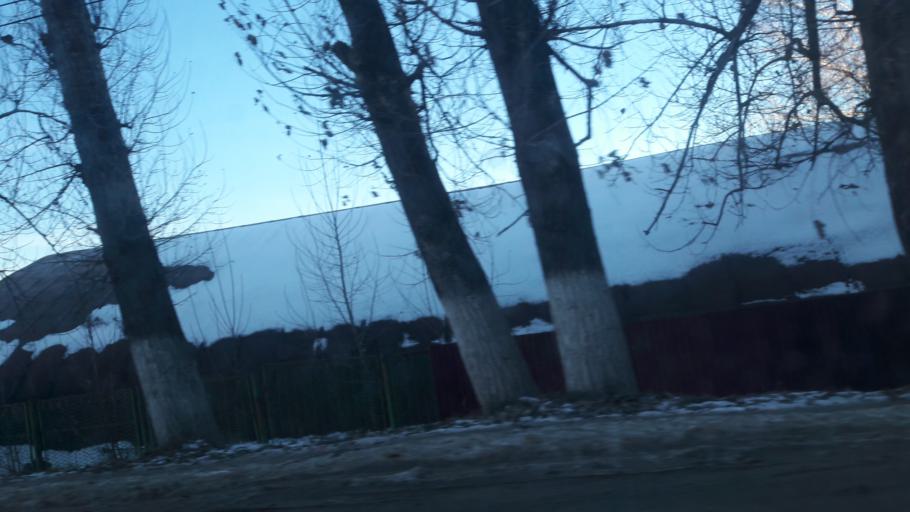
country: RU
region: Tula
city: Tula
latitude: 54.2161
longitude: 37.6468
